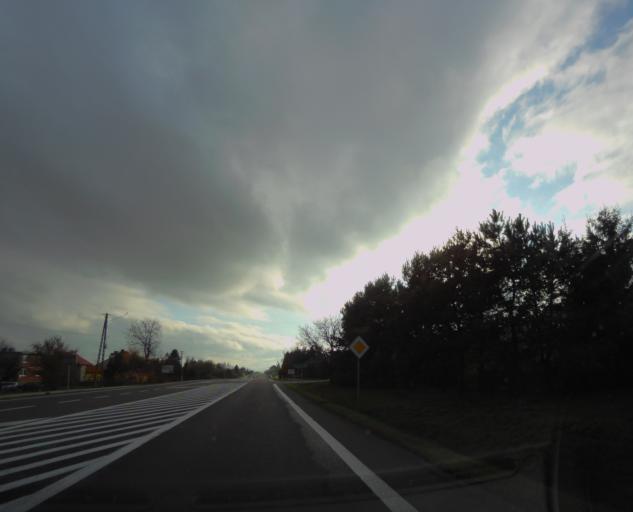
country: PL
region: Subcarpathian Voivodeship
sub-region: Powiat przemyski
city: Orly
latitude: 49.8804
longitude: 22.8139
